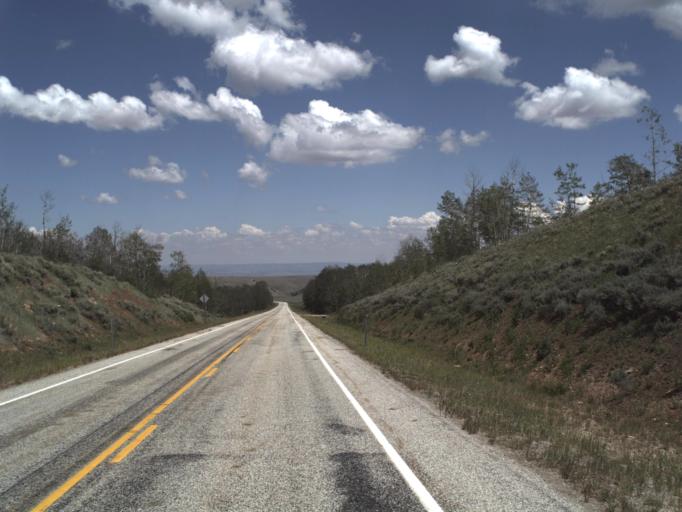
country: US
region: Utah
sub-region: Rich County
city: Randolph
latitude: 41.4730
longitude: -111.4519
